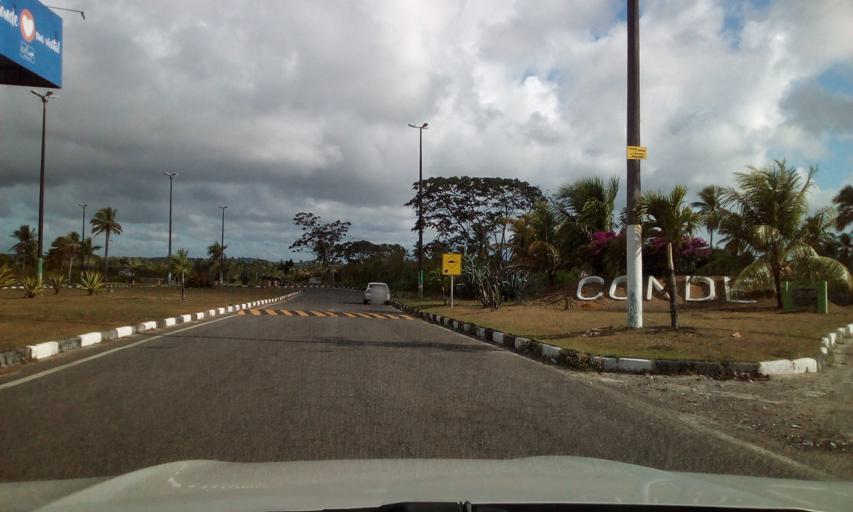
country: BR
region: Bahia
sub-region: Conde
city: Conde
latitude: -11.8259
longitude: -37.6351
